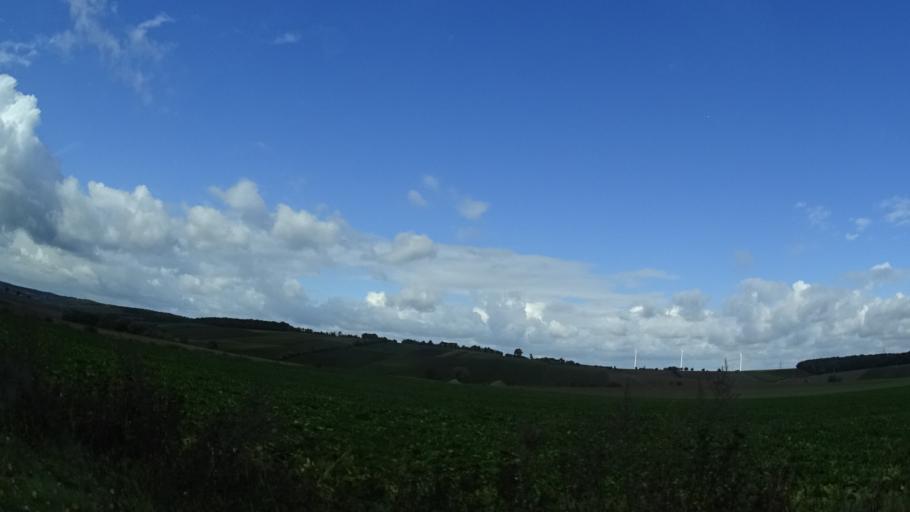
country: DE
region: Bavaria
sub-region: Regierungsbezirk Unterfranken
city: Frankenwinheim
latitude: 49.8639
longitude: 10.2837
